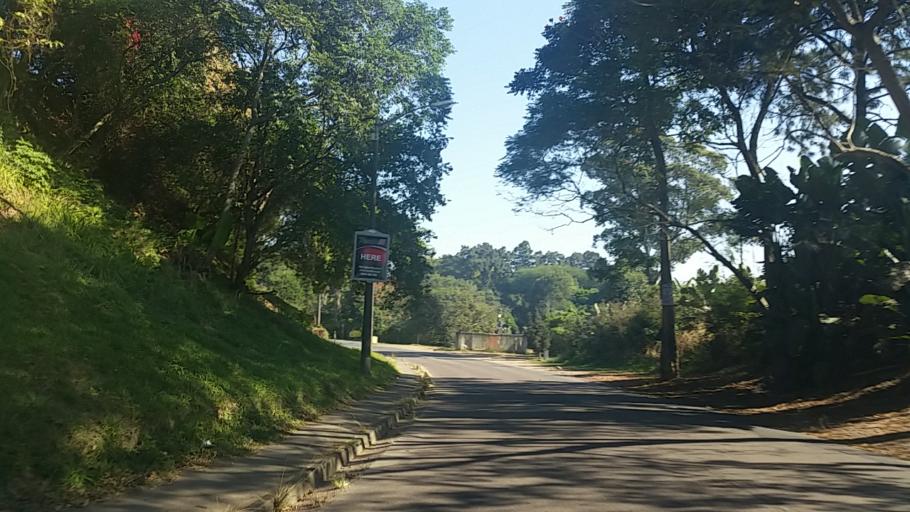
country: ZA
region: KwaZulu-Natal
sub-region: eThekwini Metropolitan Municipality
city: Berea
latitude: -29.8370
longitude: 30.9032
